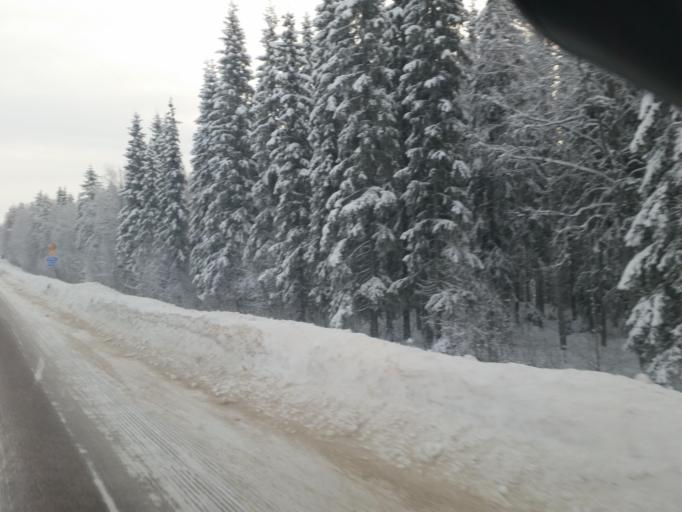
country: SE
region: Norrbotten
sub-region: Alvsbyns Kommun
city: AElvsbyn
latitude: 65.6717
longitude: 21.0798
